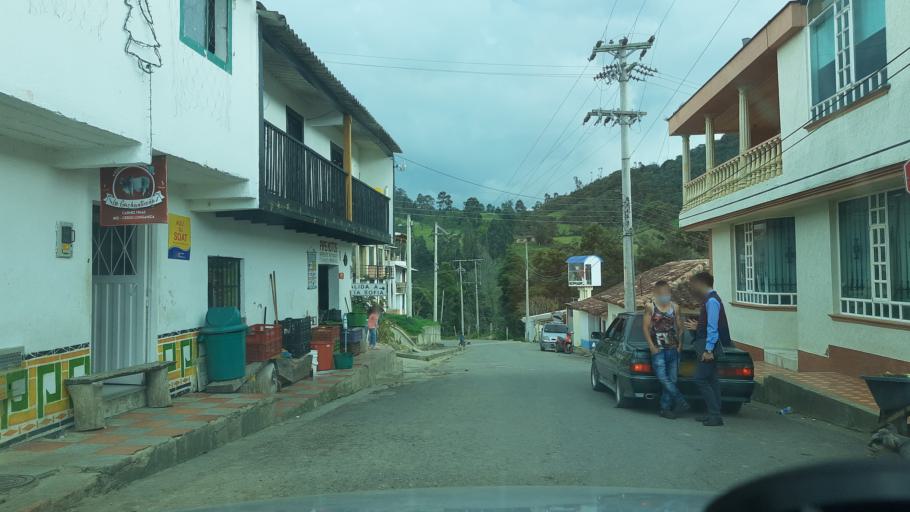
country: CO
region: Boyaca
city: Santa Sofia
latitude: 5.7511
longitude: -73.5491
